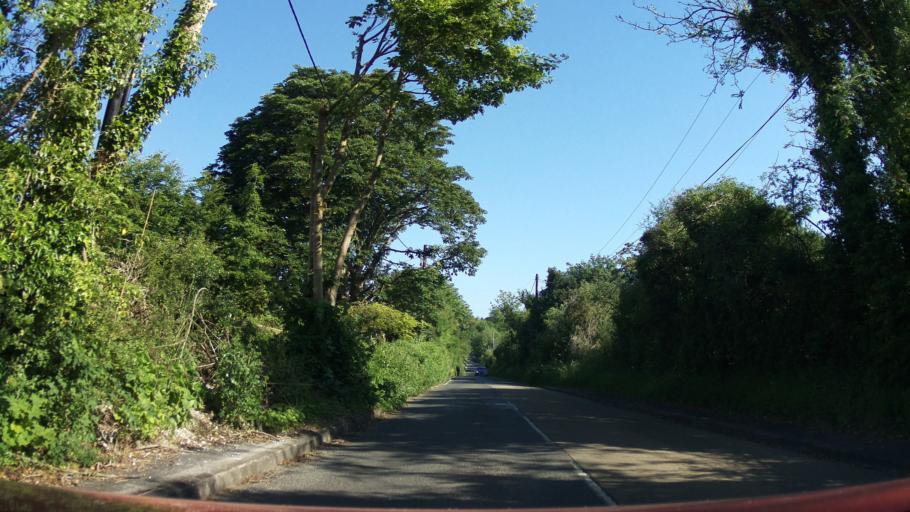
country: GB
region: England
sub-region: Hampshire
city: Winchester
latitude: 51.0846
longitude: -1.3469
